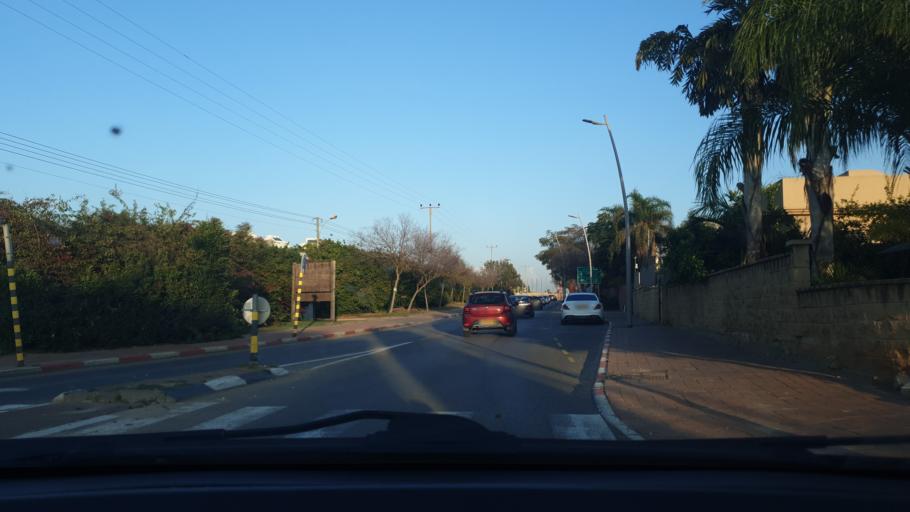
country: IL
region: Central District
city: Ramla
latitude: 31.9355
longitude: 34.8491
